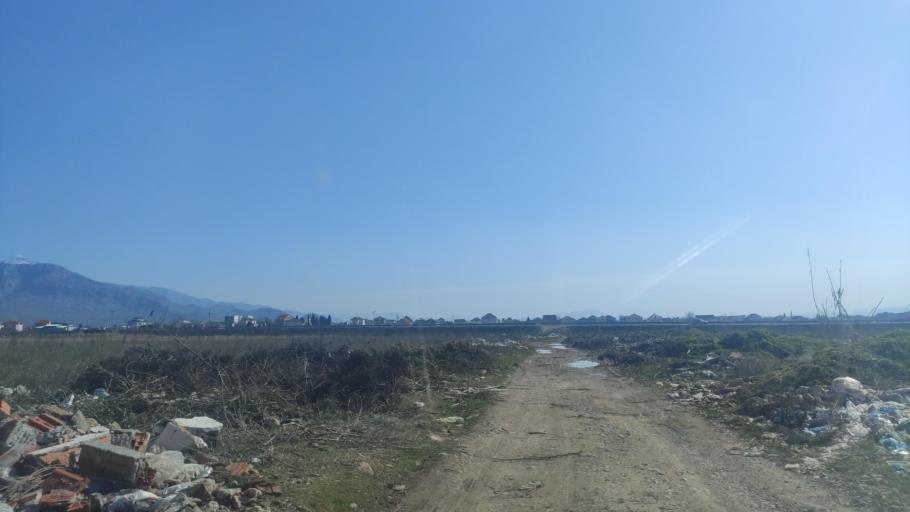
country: AL
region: Shkoder
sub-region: Rrethi i Malesia e Madhe
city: Koplik
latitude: 42.2236
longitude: 19.4346
